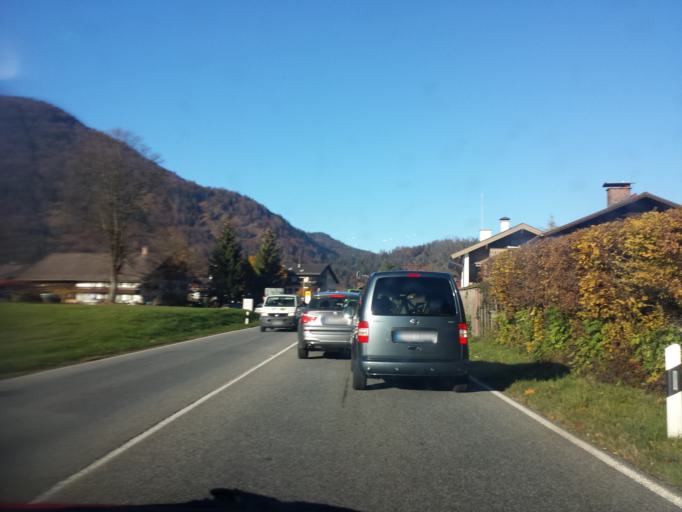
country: DE
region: Bavaria
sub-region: Upper Bavaria
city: Oberau
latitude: 47.5579
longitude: 11.1379
